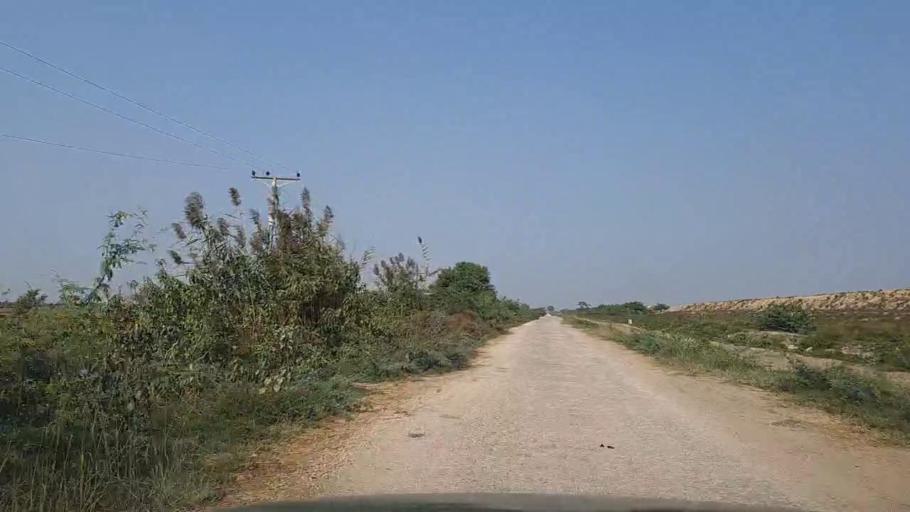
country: PK
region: Sindh
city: Chuhar Jamali
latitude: 24.5186
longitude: 67.9256
